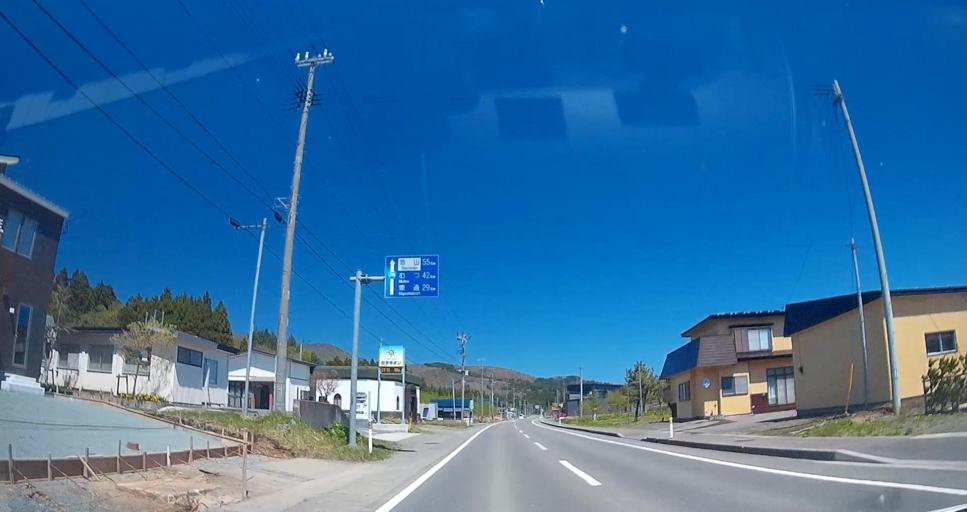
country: JP
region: Aomori
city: Mutsu
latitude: 41.0805
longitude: 141.3857
